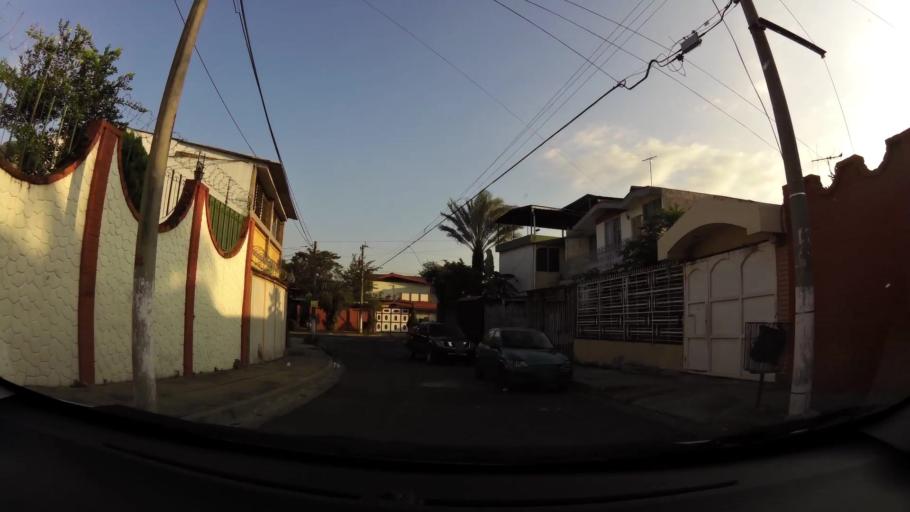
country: SV
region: San Salvador
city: Cuscatancingo
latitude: 13.7189
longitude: -89.1979
